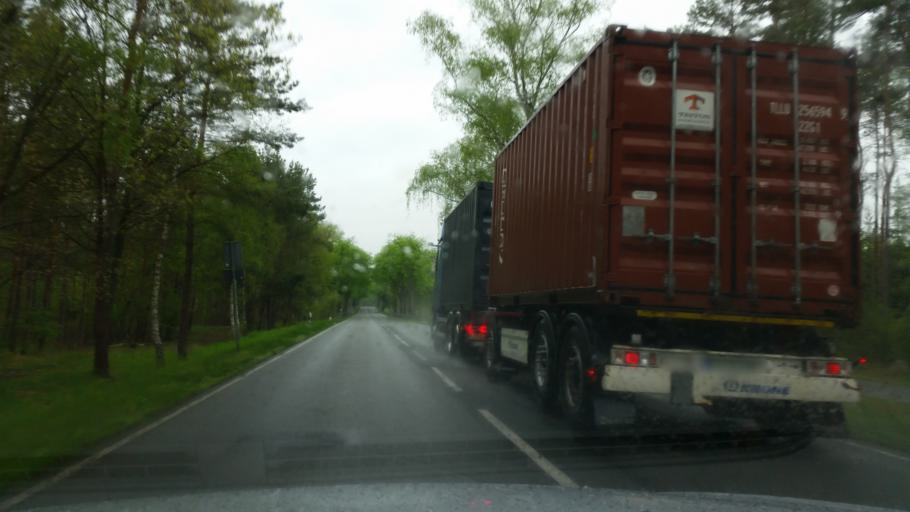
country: DE
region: Saxony-Anhalt
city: Kalbe
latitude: 52.6391
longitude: 11.3041
